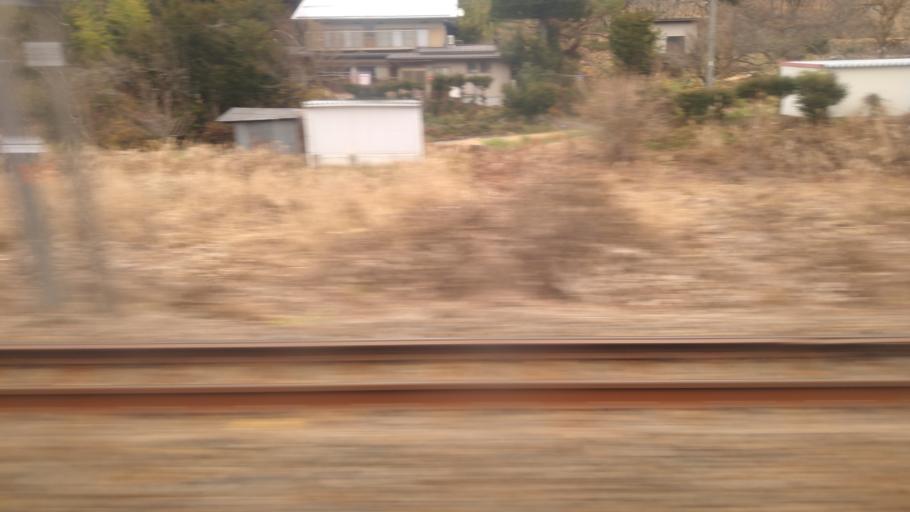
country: JP
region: Nagano
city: Ina
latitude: 35.8227
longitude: 137.6818
